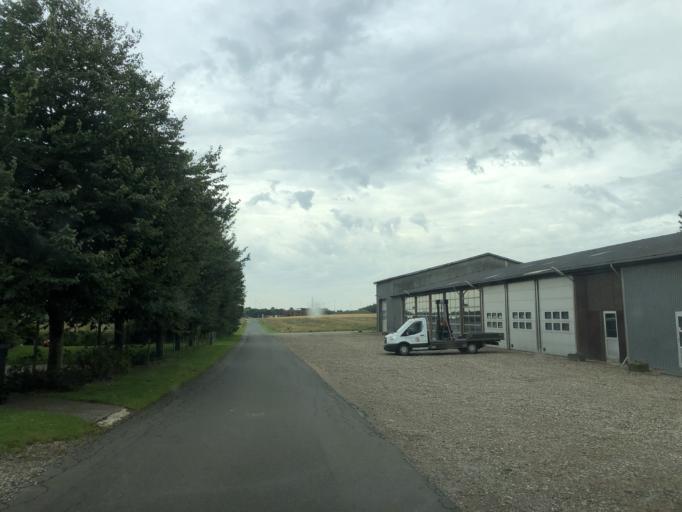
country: DK
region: Central Jutland
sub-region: Holstebro Kommune
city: Holstebro
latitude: 56.3971
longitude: 8.5830
